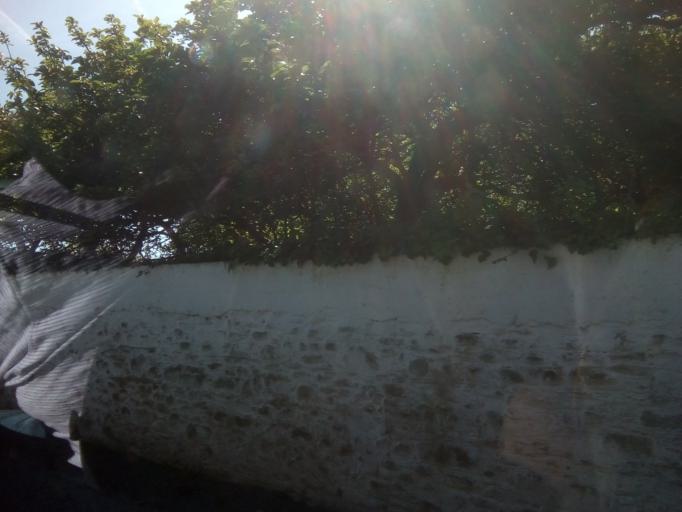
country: IE
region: Leinster
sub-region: Loch Garman
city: Loch Garman
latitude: 52.1933
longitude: -6.5479
